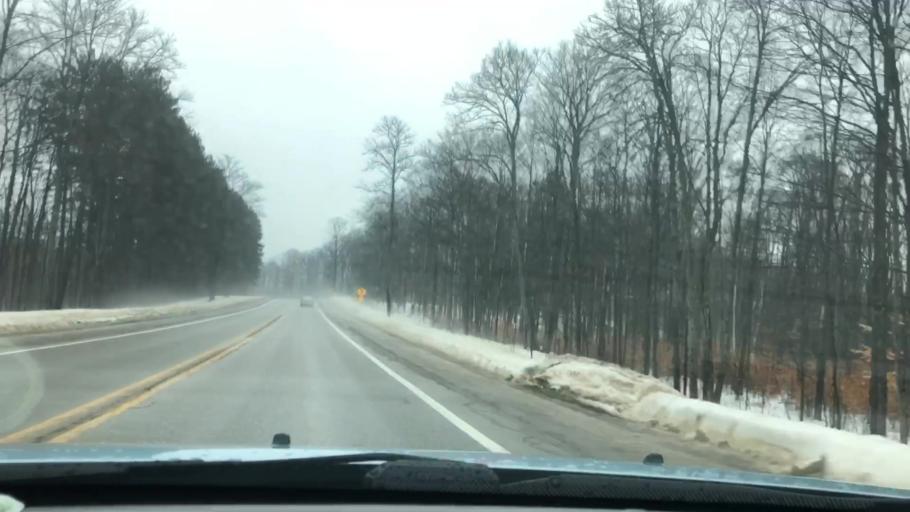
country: US
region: Michigan
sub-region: Otsego County
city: Gaylord
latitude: 45.0607
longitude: -84.7971
